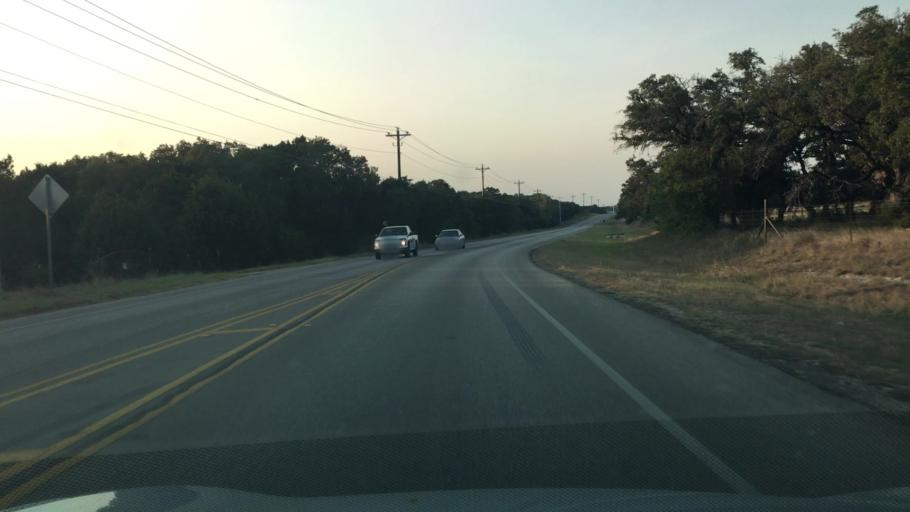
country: US
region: Texas
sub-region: Hays County
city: Dripping Springs
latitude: 30.1547
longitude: -98.0091
